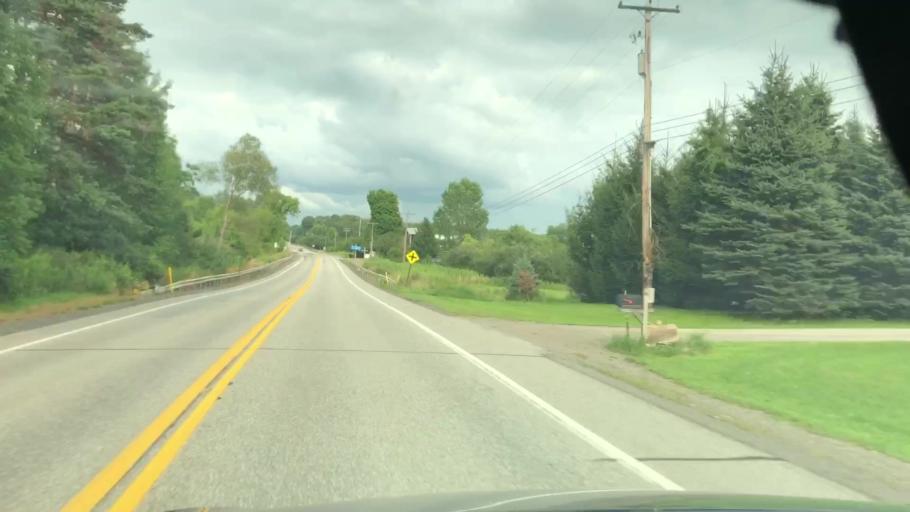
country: US
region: Pennsylvania
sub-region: Erie County
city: Northwest Harborcreek
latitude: 42.0569
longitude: -79.8965
